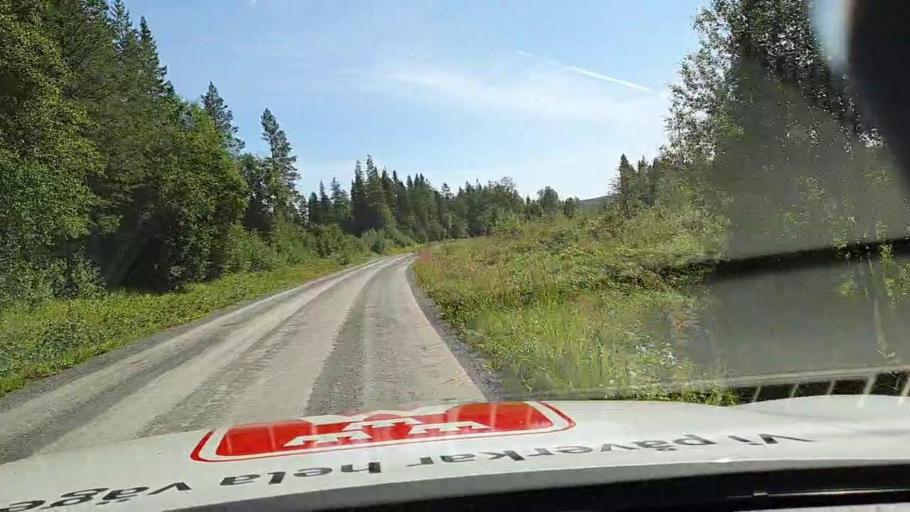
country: SE
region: Jaemtland
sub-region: Krokoms Kommun
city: Krokom
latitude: 63.6833
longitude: 14.5785
